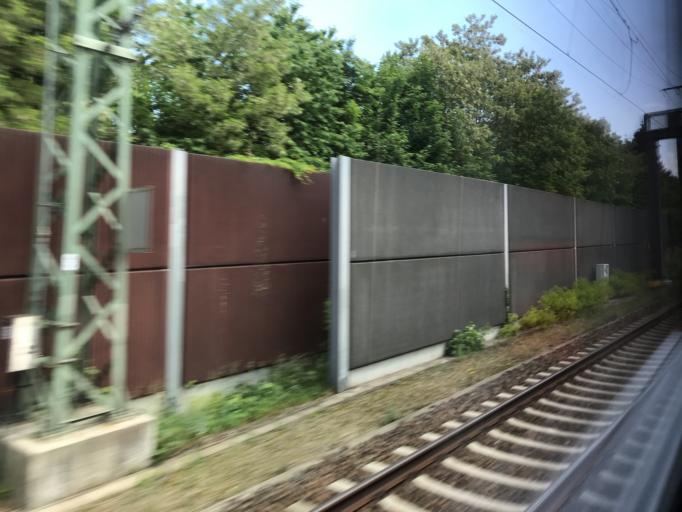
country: DE
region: Bavaria
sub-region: Swabia
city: Neu-Ulm
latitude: 48.3982
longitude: 10.0195
